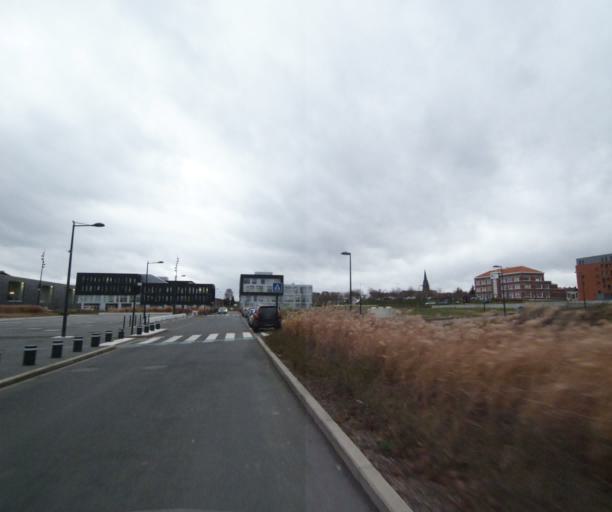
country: FR
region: Nord-Pas-de-Calais
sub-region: Departement du Nord
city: Anzin
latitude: 50.3749
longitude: 3.5208
